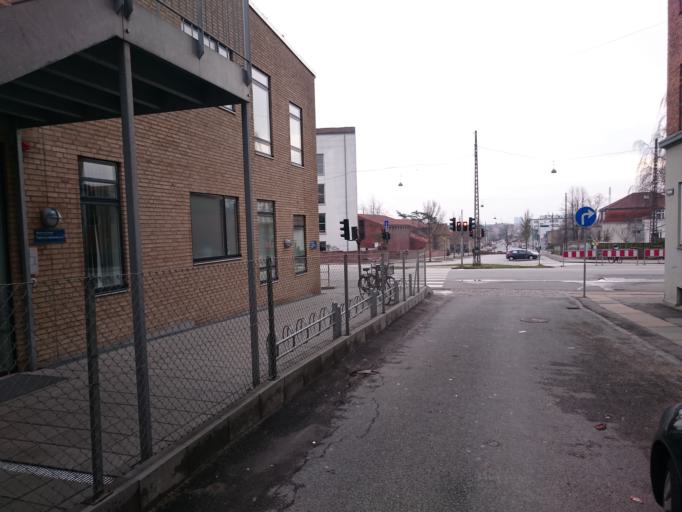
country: DK
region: Capital Region
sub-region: Kobenhavn
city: Vanlose
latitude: 55.6973
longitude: 12.5060
